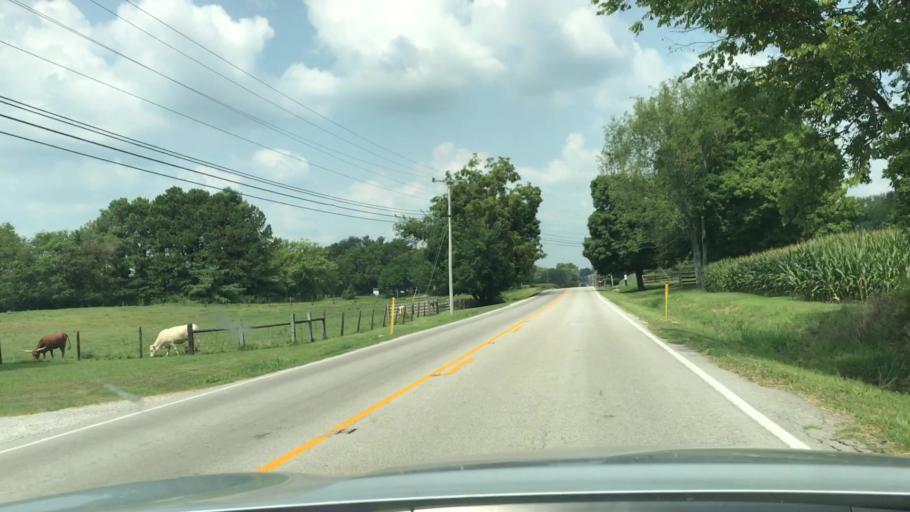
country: US
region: Kentucky
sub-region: Todd County
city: Elkton
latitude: 36.8063
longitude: -87.1331
